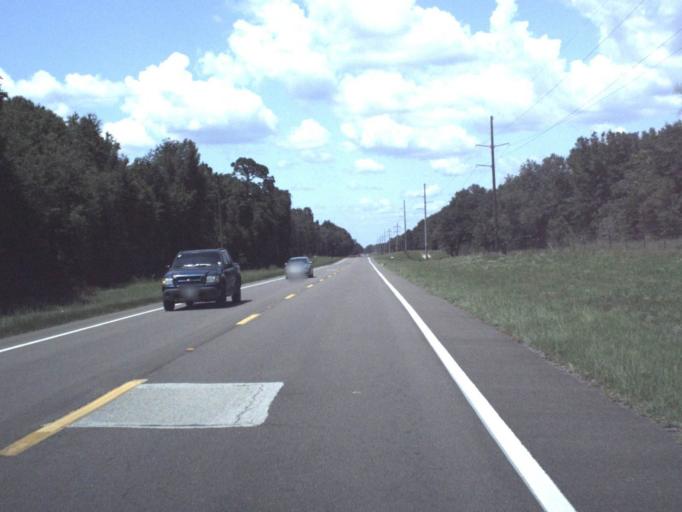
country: US
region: Florida
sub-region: Gilchrist County
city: Trenton
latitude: 29.7095
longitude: -82.7545
